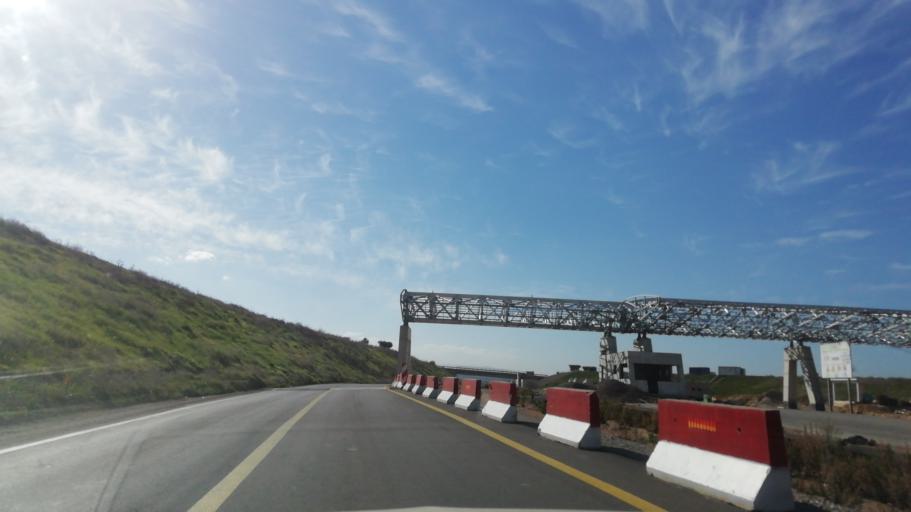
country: DZ
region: Tlemcen
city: Bensekrane
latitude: 34.9839
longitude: -1.2177
